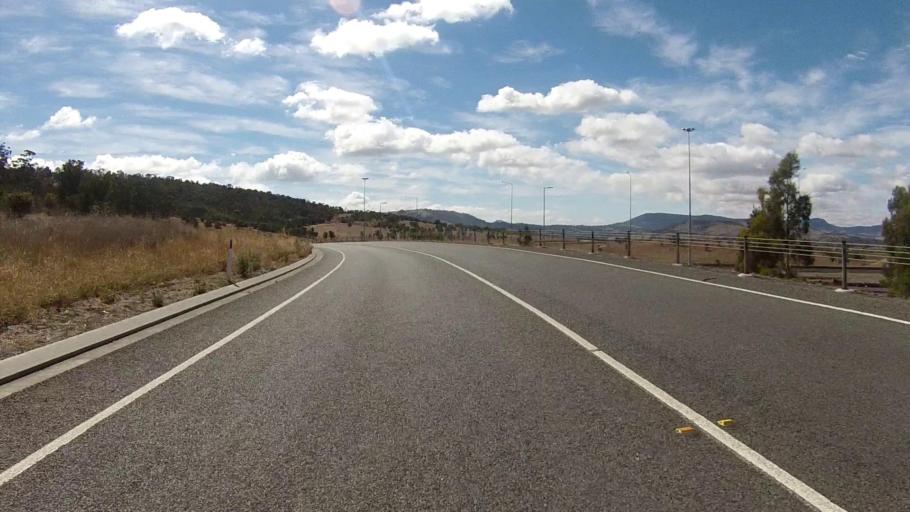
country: AU
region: Tasmania
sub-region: Brighton
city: Bridgewater
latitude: -42.7120
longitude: 147.2309
